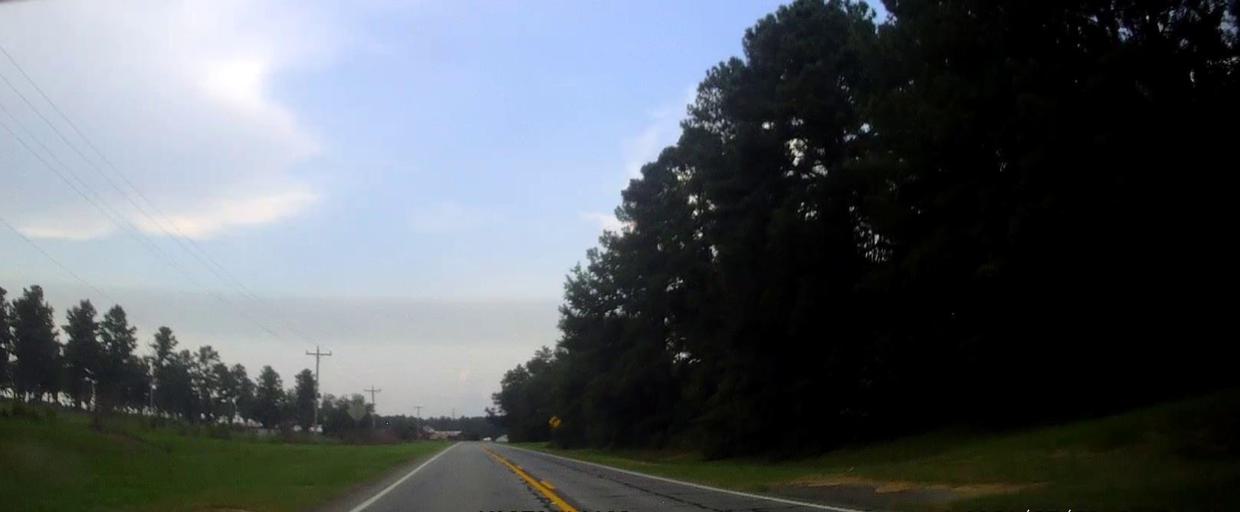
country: US
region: Georgia
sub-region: Laurens County
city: East Dublin
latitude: 32.5759
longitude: -82.8384
